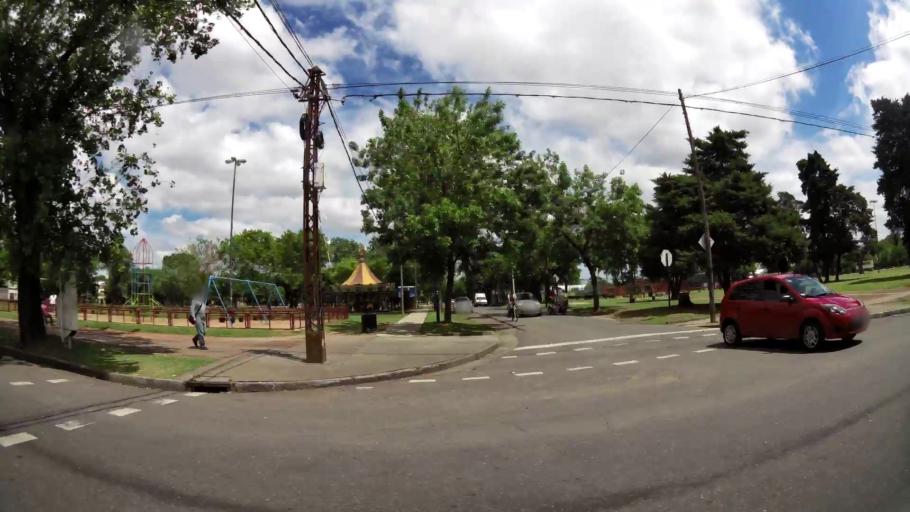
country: AR
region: Santa Fe
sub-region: Departamento de Rosario
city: Rosario
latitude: -32.9717
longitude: -60.6342
